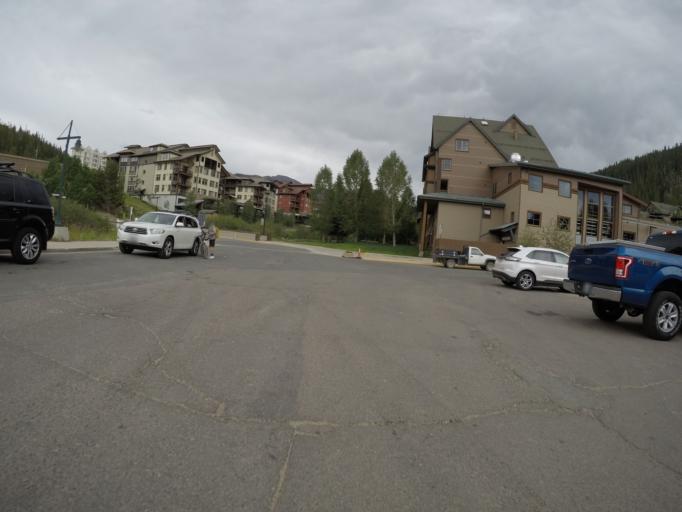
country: US
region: Colorado
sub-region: Grand County
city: Fraser
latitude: 39.8866
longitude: -105.7621
